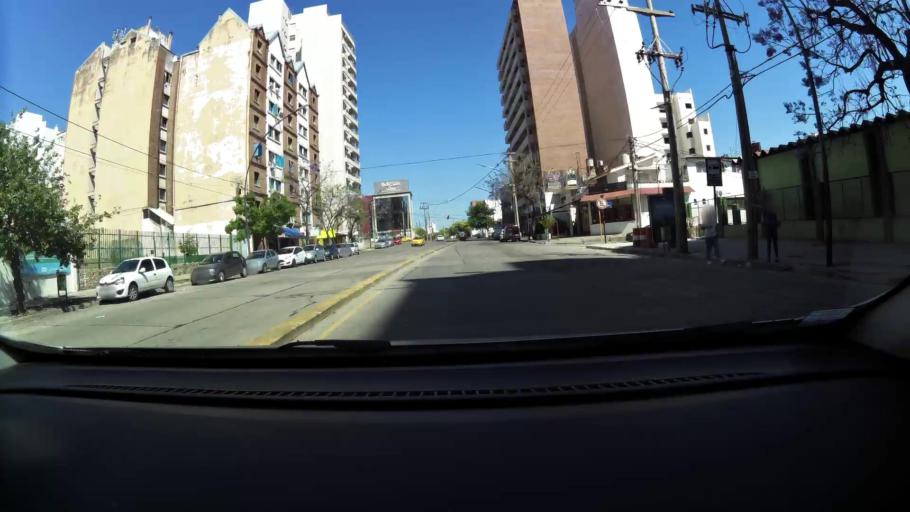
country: AR
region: Cordoba
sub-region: Departamento de Capital
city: Cordoba
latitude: -31.4175
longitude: -64.1985
